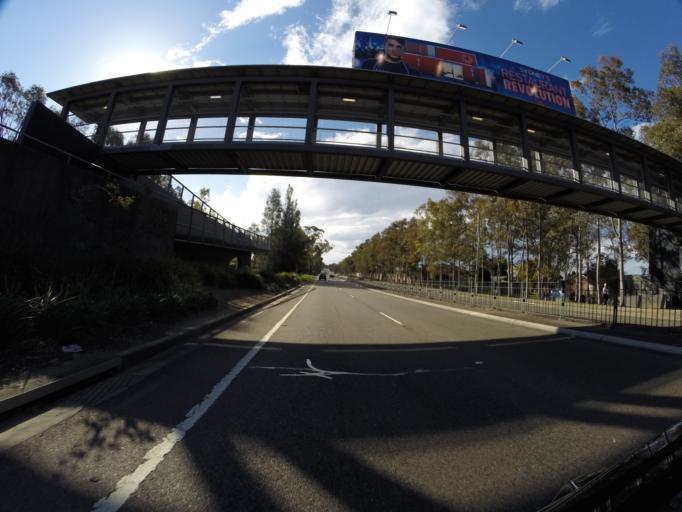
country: AU
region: New South Wales
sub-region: Fairfield
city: Cecil Park
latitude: -33.8724
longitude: 150.8699
